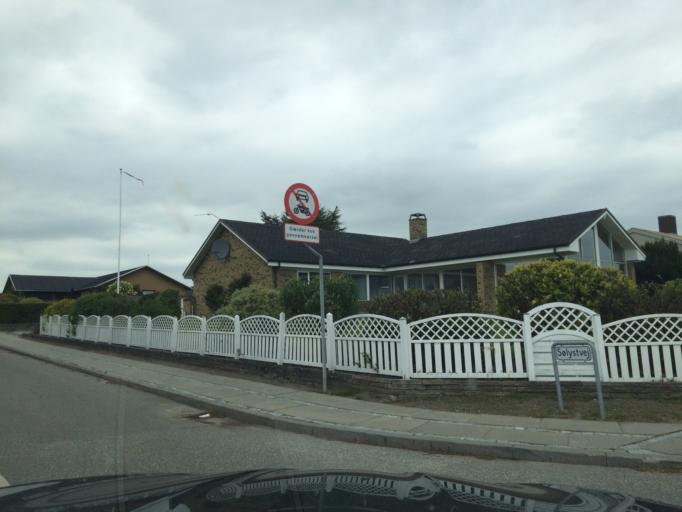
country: DK
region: Central Jutland
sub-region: Arhus Kommune
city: Hjortshoj
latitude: 56.2121
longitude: 10.2873
